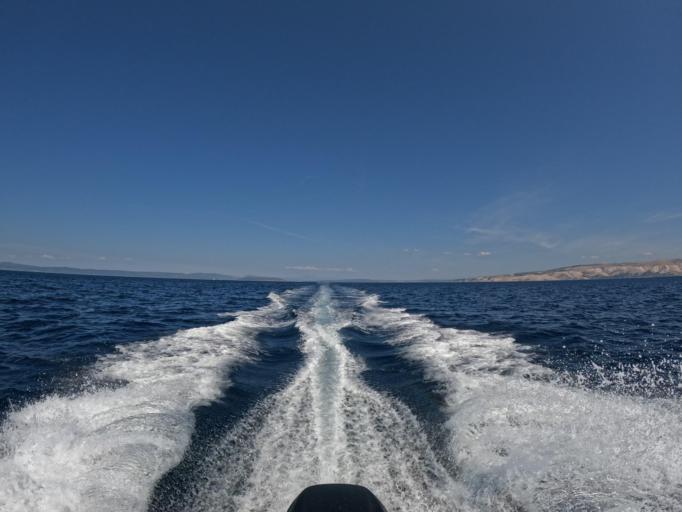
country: HR
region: Primorsko-Goranska
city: Lopar
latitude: 44.8902
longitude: 14.6454
